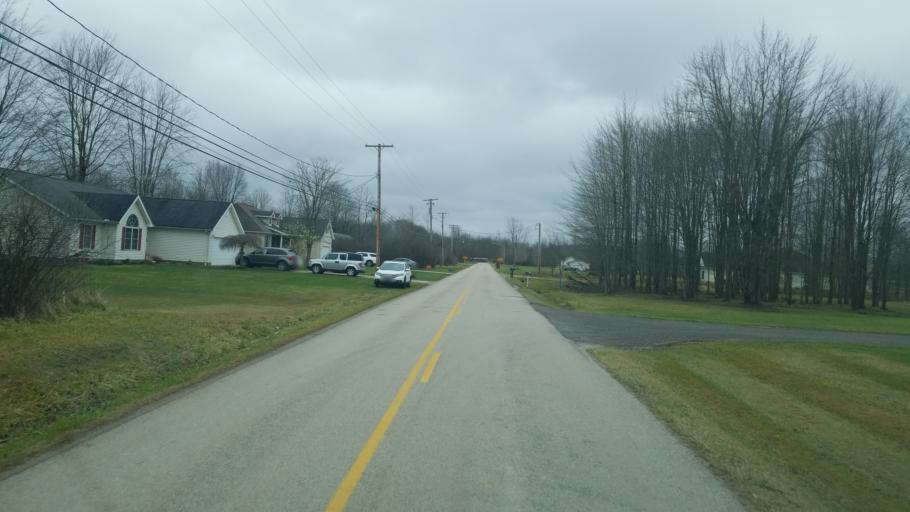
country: US
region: Ohio
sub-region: Ashtabula County
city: Roaming Shores
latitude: 41.6395
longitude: -80.8360
